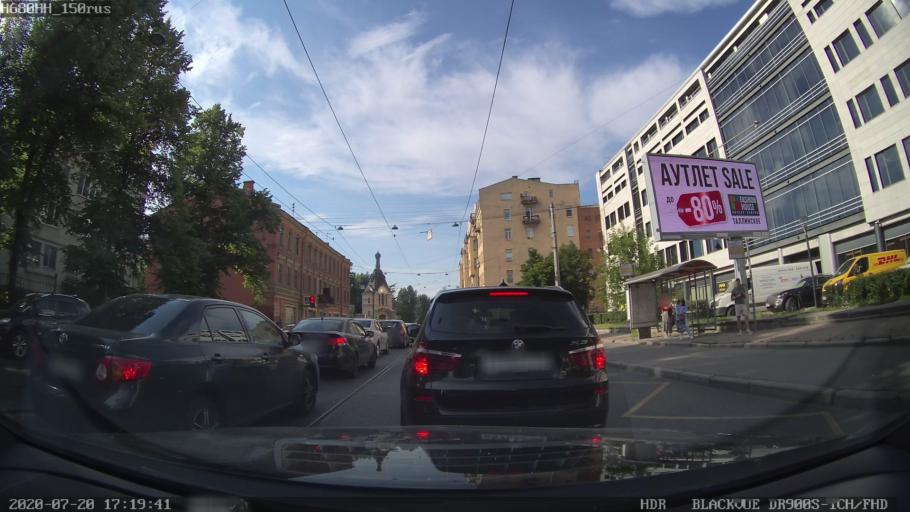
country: RU
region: St.-Petersburg
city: Admiralteisky
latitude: 59.9052
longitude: 30.2771
